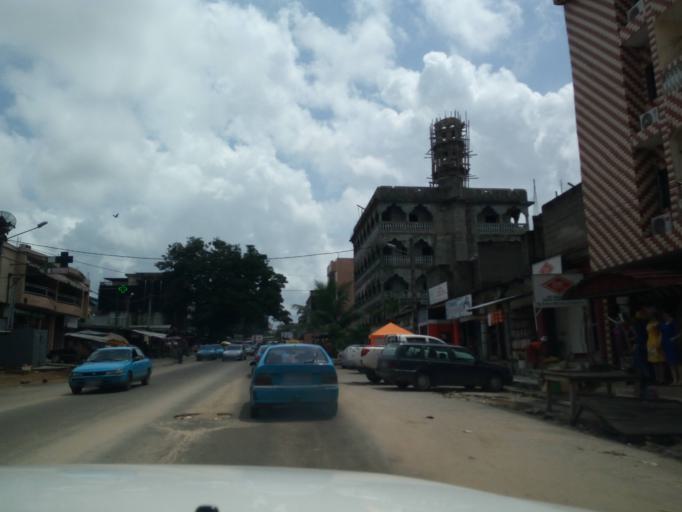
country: CI
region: Lagunes
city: Abidjan
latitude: 5.3399
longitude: -4.0972
